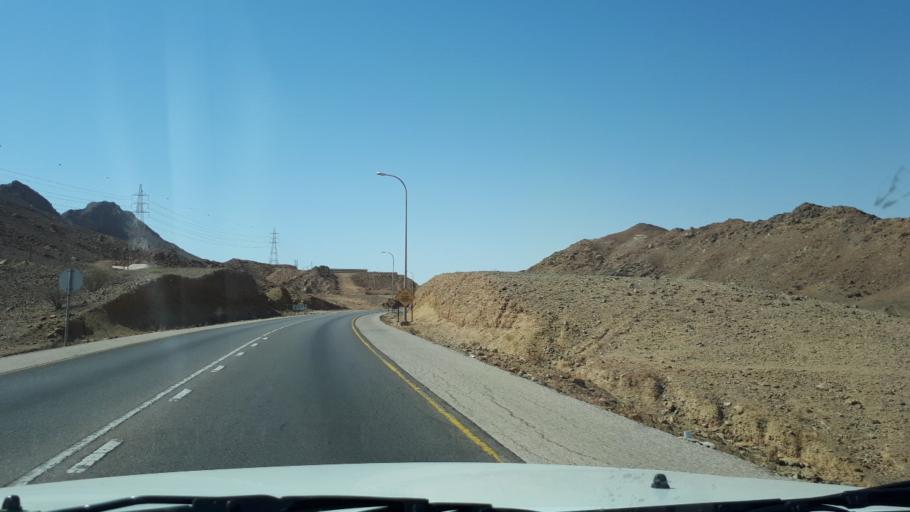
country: OM
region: Ash Sharqiyah
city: Sur
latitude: 22.3293
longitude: 59.3079
